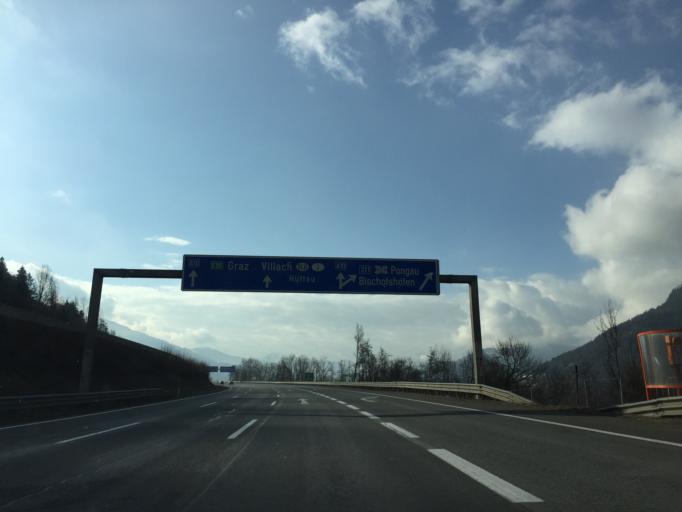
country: AT
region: Salzburg
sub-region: Politischer Bezirk Sankt Johann im Pongau
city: Pfarrwerfen
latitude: 47.4469
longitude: 13.2179
